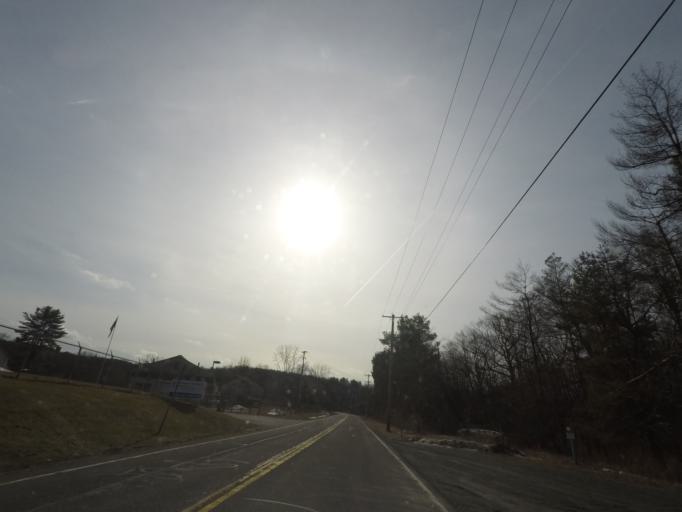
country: US
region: New York
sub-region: Rensselaer County
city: Nassau
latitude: 42.4829
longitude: -73.5645
